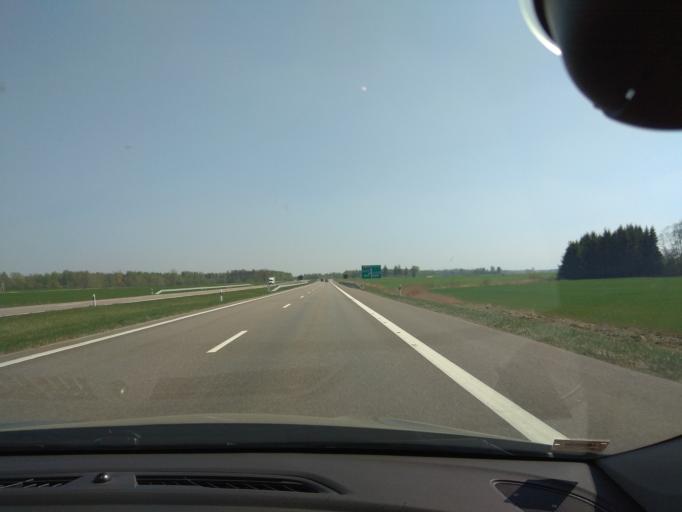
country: LT
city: Ramygala
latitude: 55.5435
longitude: 24.5316
